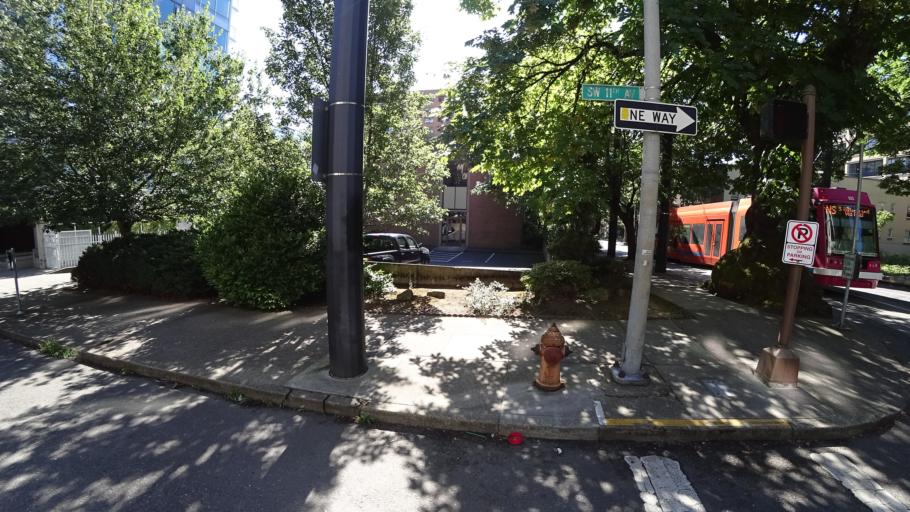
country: US
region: Oregon
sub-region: Multnomah County
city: Portland
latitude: 45.5144
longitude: -122.6863
